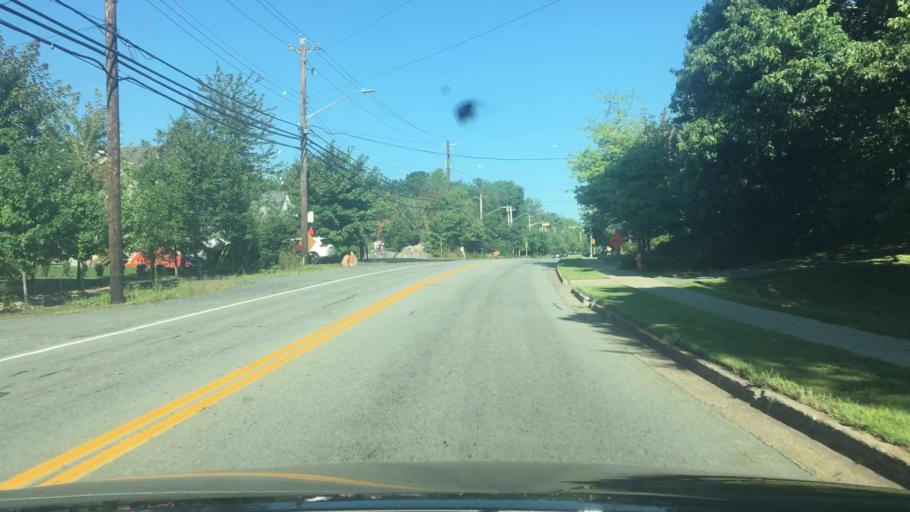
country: CA
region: Nova Scotia
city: Dartmouth
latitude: 44.7161
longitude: -63.6814
